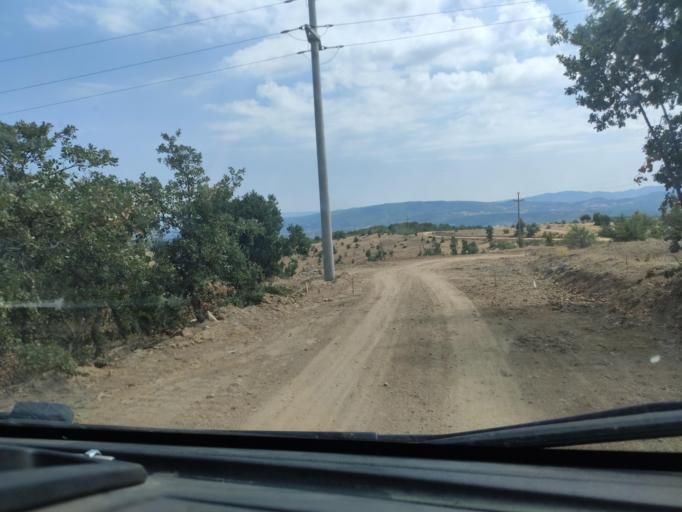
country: MK
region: Radovis
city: Radovish
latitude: 41.6705
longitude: 22.4052
